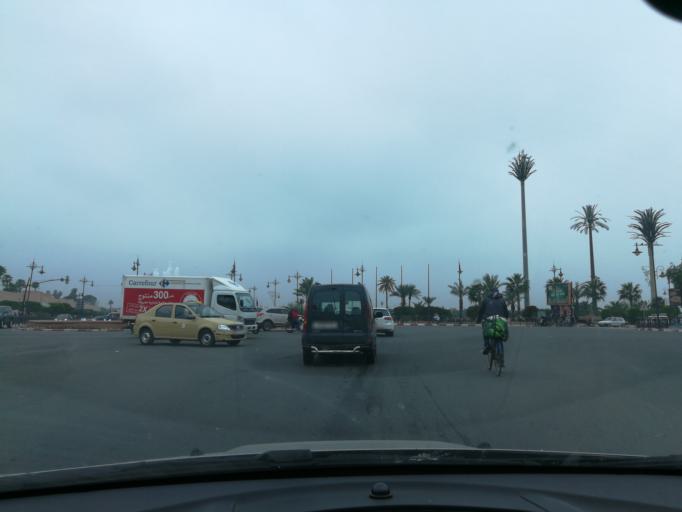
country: MA
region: Marrakech-Tensift-Al Haouz
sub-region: Marrakech
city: Marrakesh
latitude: 31.6221
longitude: -7.9993
